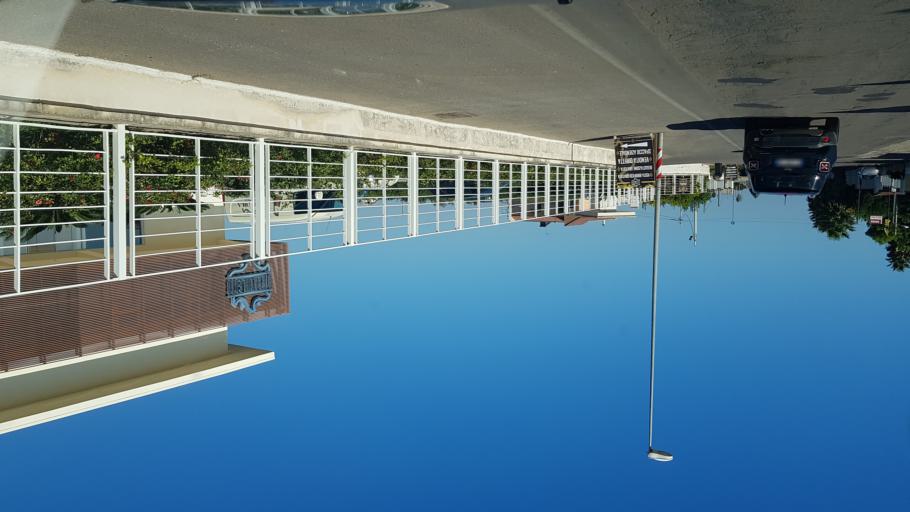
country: IT
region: Apulia
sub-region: Provincia di Lecce
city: Leverano
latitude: 40.2985
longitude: 18.0046
